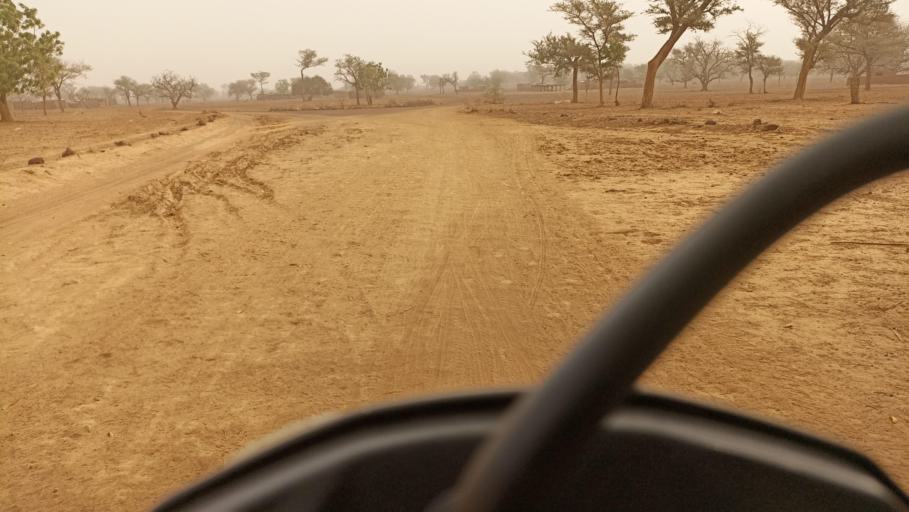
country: BF
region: Nord
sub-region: Province du Zondoma
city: Gourcy
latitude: 13.2929
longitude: -2.5212
